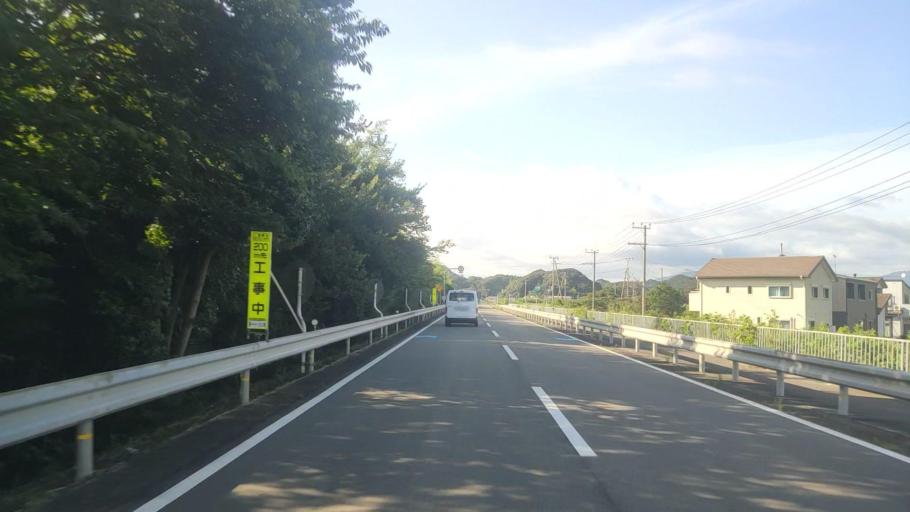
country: JP
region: Wakayama
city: Tanabe
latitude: 33.6751
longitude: 135.4077
